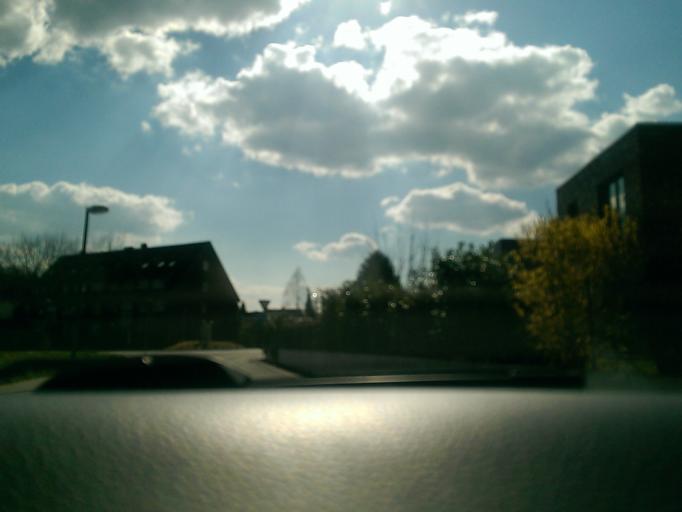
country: DE
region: North Rhine-Westphalia
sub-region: Regierungsbezirk Munster
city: Muenster
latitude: 51.9342
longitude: 7.6723
